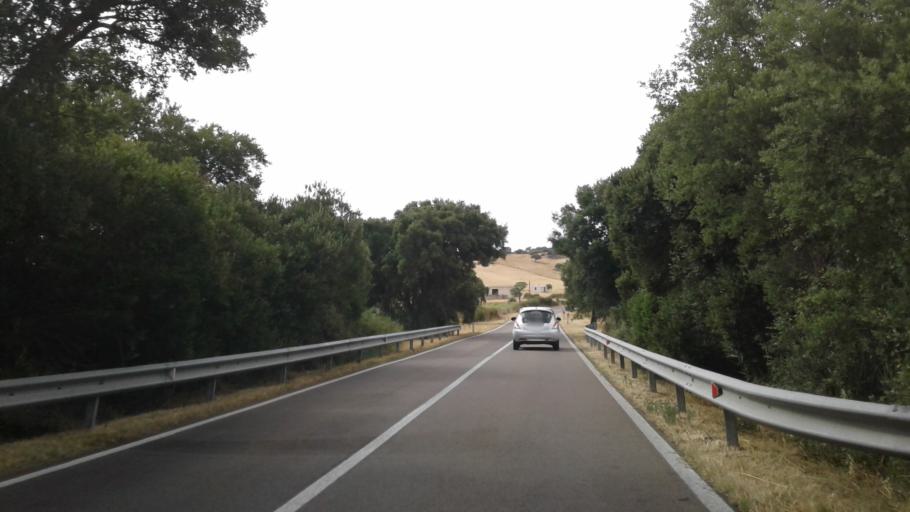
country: IT
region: Sardinia
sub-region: Provincia di Olbia-Tempio
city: Sant'Antonio di Gallura
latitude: 40.9504
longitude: 9.2956
